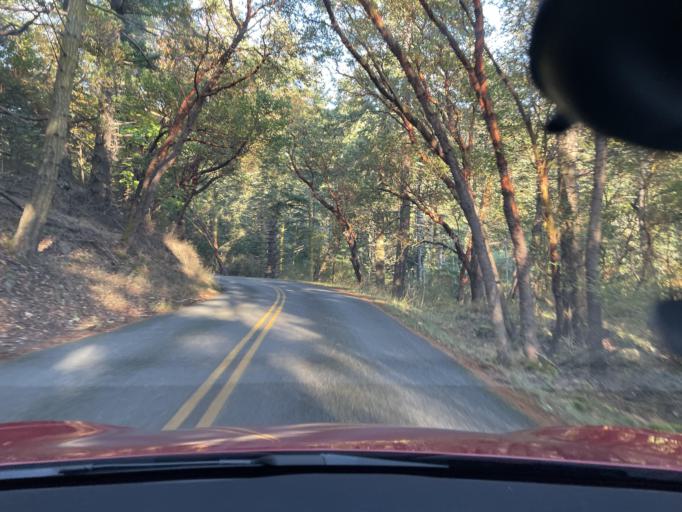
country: US
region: Washington
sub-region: San Juan County
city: Friday Harbor
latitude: 48.5147
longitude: -123.1450
